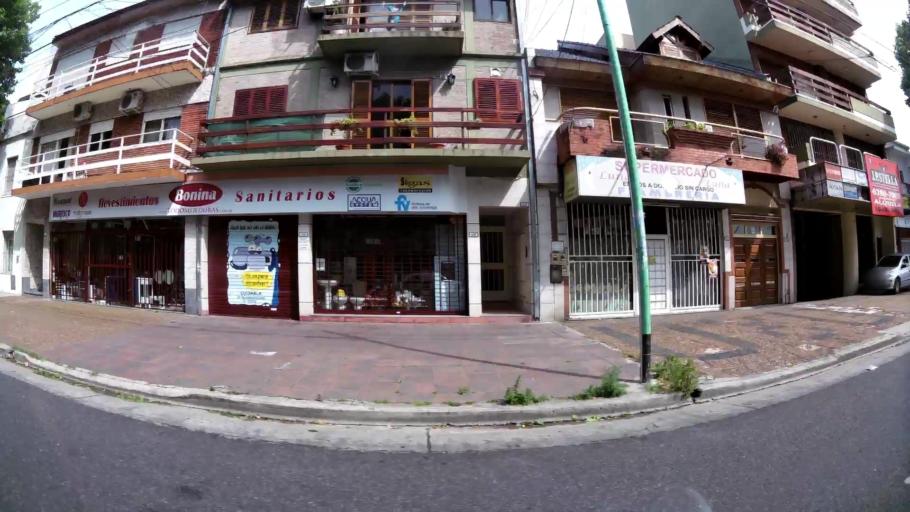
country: AR
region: Buenos Aires F.D.
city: Villa Santa Rita
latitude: -34.6475
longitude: -58.5057
